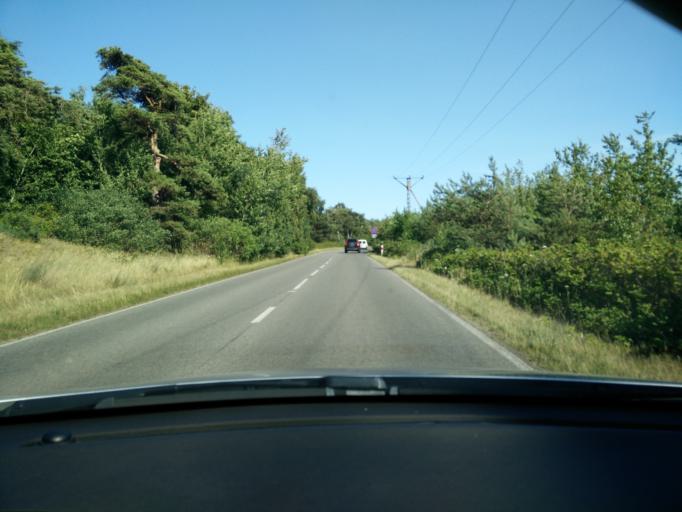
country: PL
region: Pomeranian Voivodeship
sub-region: Powiat pucki
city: Jastarnia
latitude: 54.7272
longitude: 18.6018
